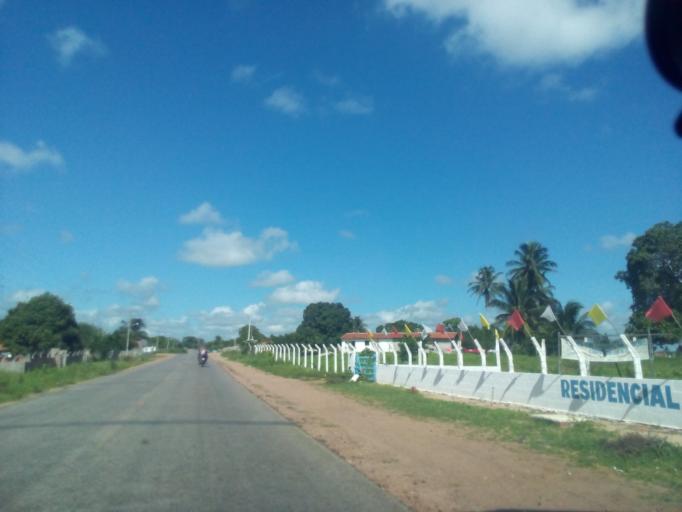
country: BR
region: Rio Grande do Norte
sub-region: Sao Paulo Do Potengi
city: Sao Paulo do Potengi
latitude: -5.9140
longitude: -35.7070
